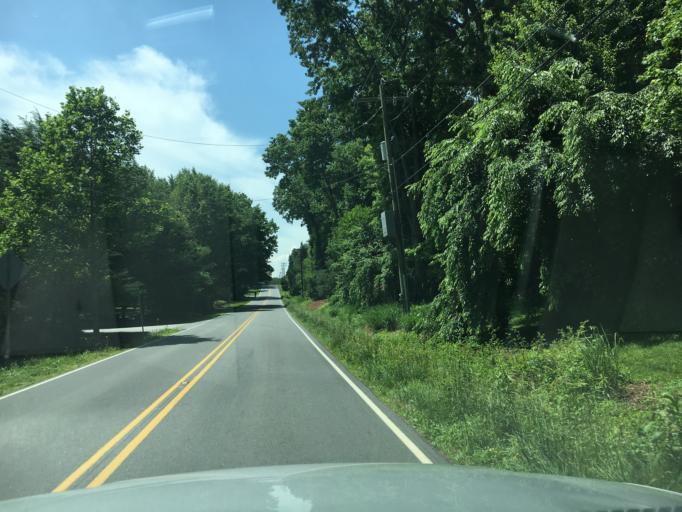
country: US
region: North Carolina
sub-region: Henderson County
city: Mountain Home
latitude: 35.3840
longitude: -82.5194
